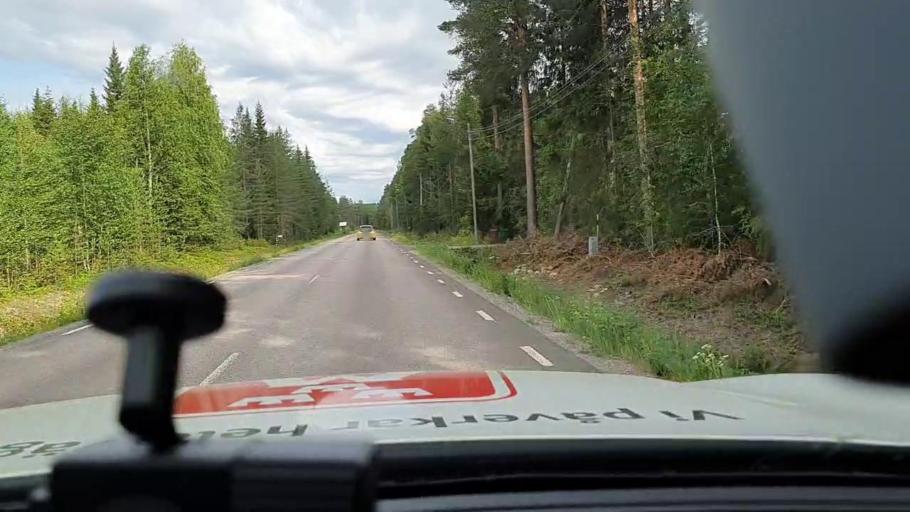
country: SE
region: Norrbotten
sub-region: Bodens Kommun
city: Saevast
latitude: 65.7268
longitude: 21.7460
